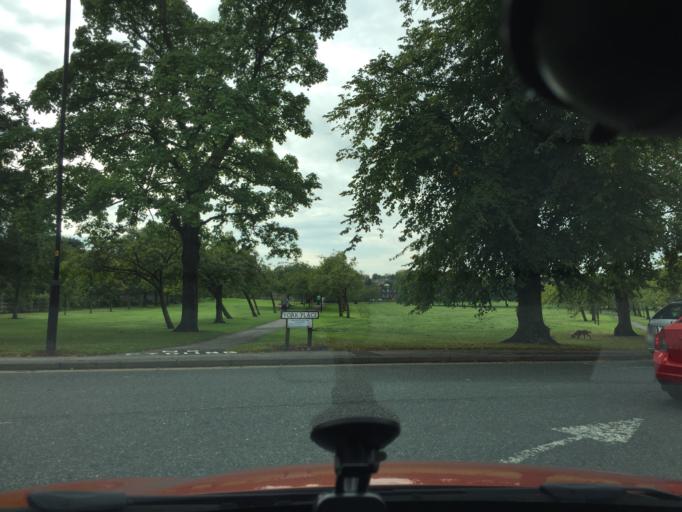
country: GB
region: England
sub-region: North Yorkshire
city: Harrogate
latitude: 53.9885
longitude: -1.5356
